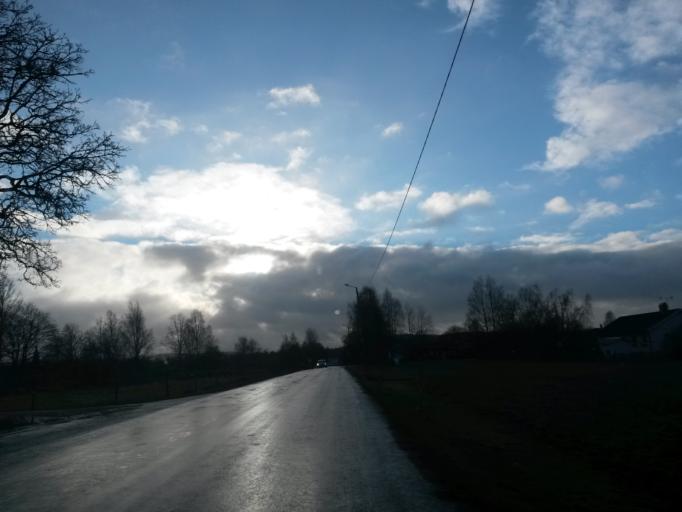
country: SE
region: Vaestra Goetaland
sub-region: Boras Kommun
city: Boras
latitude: 57.8628
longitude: 12.9299
